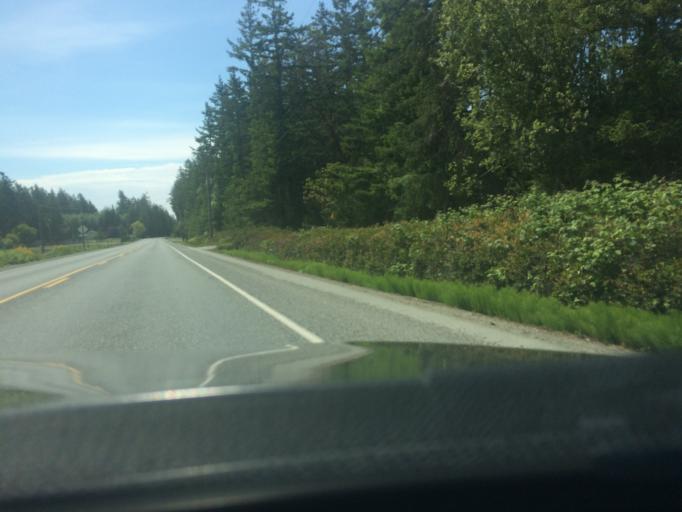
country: US
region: Washington
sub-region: Skagit County
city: Anacortes
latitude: 48.4328
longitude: -122.6642
